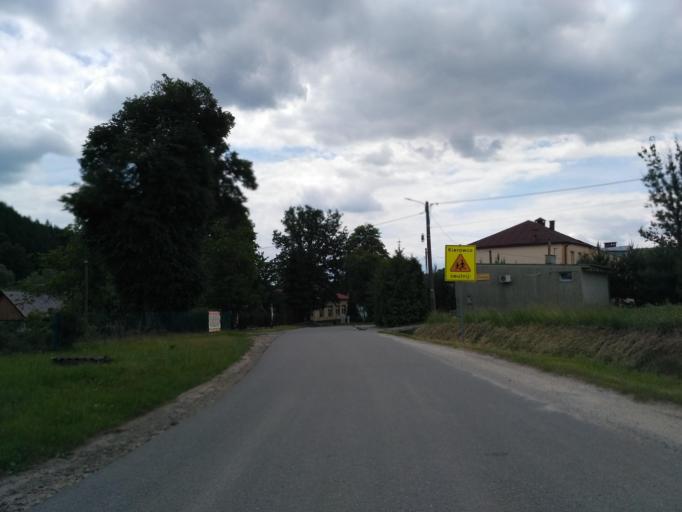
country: PL
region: Subcarpathian Voivodeship
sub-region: Powiat przeworski
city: Jawornik Polski
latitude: 49.8570
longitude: 22.2878
